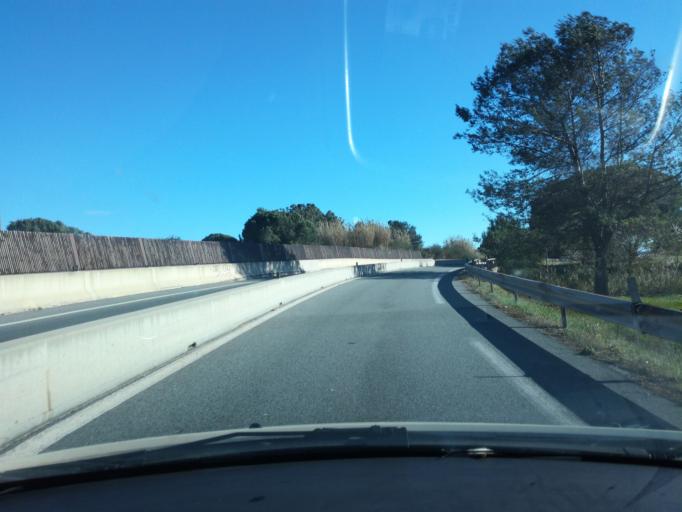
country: FR
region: Provence-Alpes-Cote d'Azur
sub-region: Departement du Var
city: Puget-sur-Argens
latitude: 43.4602
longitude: 6.6888
